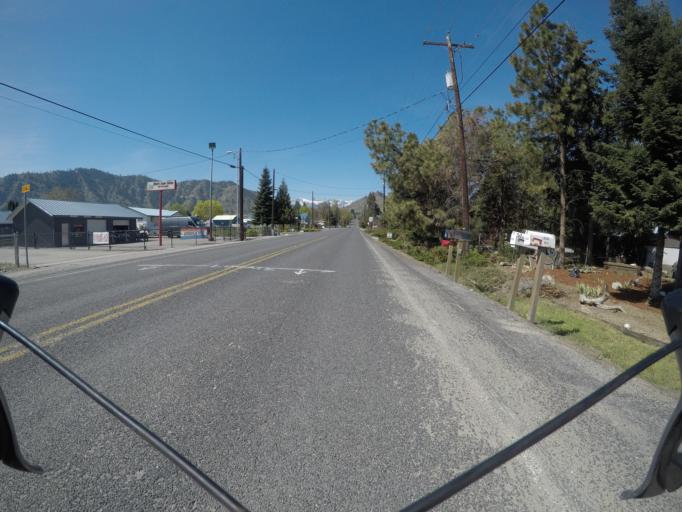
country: US
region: Washington
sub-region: Chelan County
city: Cashmere
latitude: 47.5246
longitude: -120.4886
